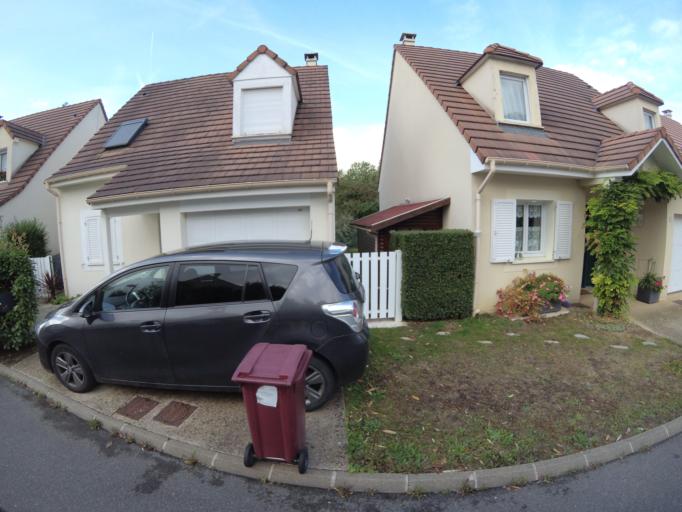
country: FR
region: Ile-de-France
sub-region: Departement de Seine-et-Marne
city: Montevrain
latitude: 48.8700
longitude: 2.7530
